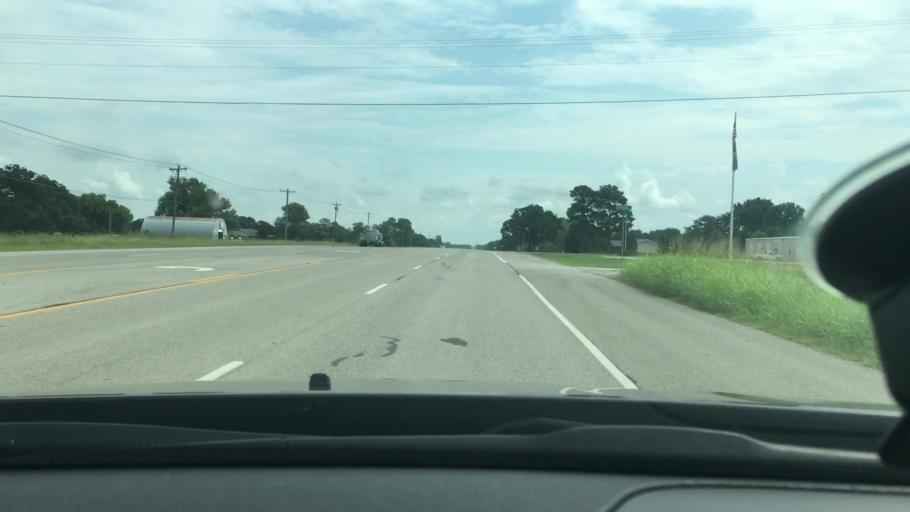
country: US
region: Oklahoma
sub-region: Carter County
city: Dickson
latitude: 34.1871
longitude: -96.9989
